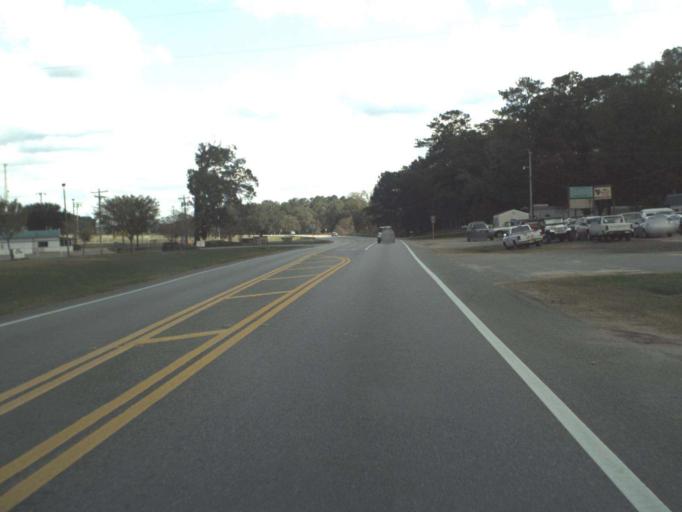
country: US
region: Florida
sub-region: Jackson County
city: Sneads
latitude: 30.7098
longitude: -84.9138
